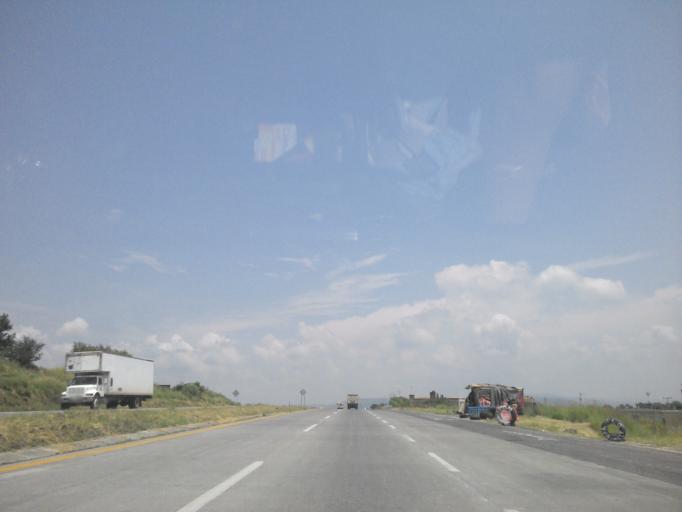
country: MX
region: Jalisco
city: Puente Grande
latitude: 20.5743
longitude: -103.1631
